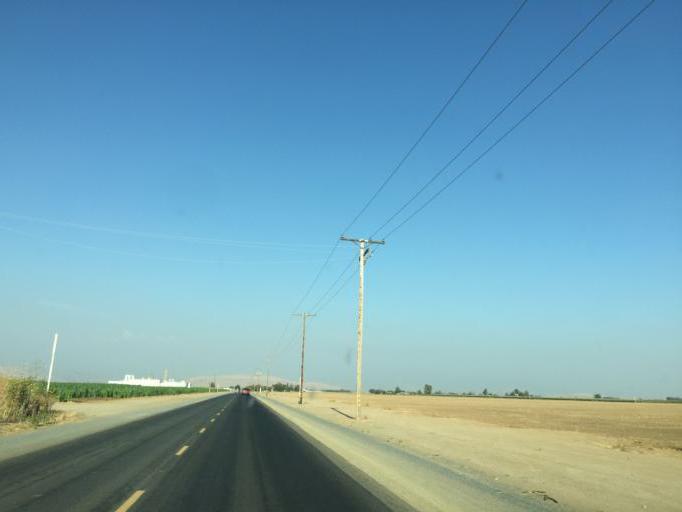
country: US
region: California
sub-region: Tulare County
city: Cutler
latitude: 36.4580
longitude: -119.3111
